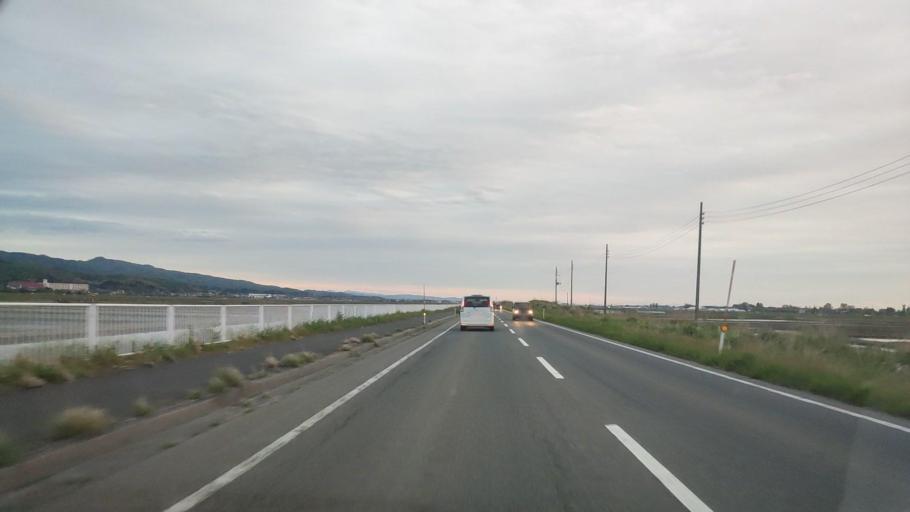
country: JP
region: Niigata
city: Niitsu-honcho
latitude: 37.7689
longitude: 139.1012
